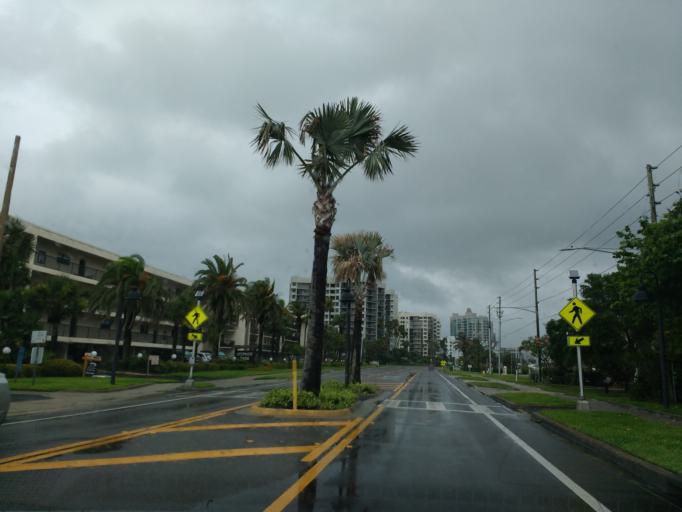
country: US
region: Florida
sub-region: Pinellas County
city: Belleair Beach
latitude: 27.9352
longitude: -82.8401
